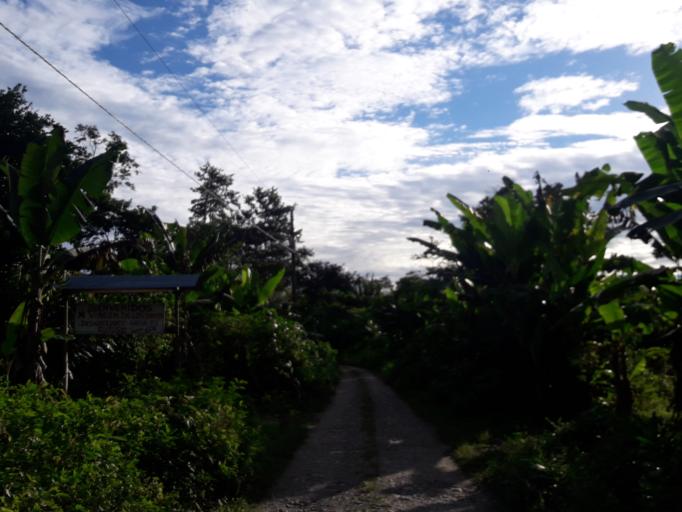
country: EC
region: Orellana
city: Boca Suno
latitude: -0.8898
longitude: -77.3047
